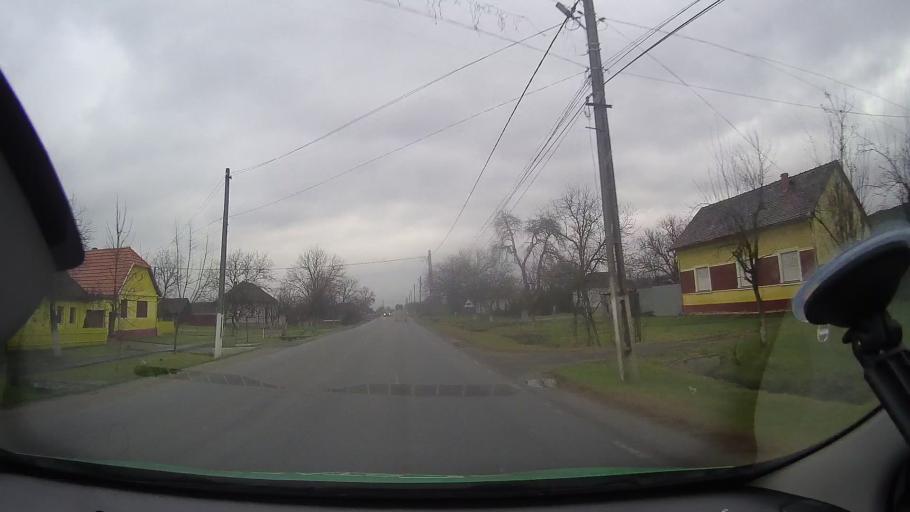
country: RO
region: Arad
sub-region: Comuna Almas
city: Almas
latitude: 46.2825
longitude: 22.2694
